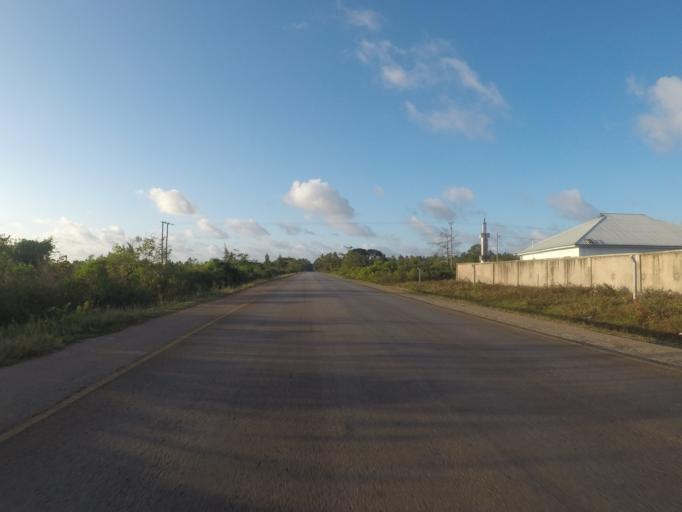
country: TZ
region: Zanzibar Central/South
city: Koani
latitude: -6.1643
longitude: 39.3301
